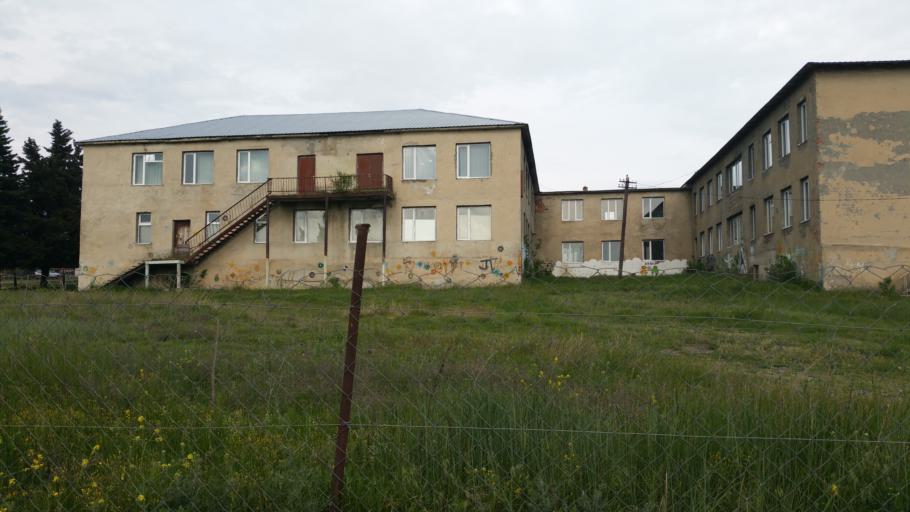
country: AZ
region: Agstafa
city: Saloglu
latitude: 41.5052
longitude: 45.3767
